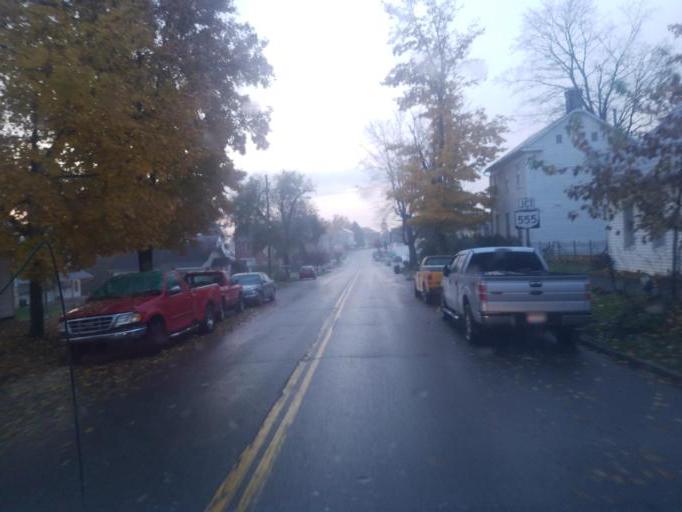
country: US
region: Ohio
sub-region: Morgan County
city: McConnelsville
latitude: 39.4914
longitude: -81.8650
